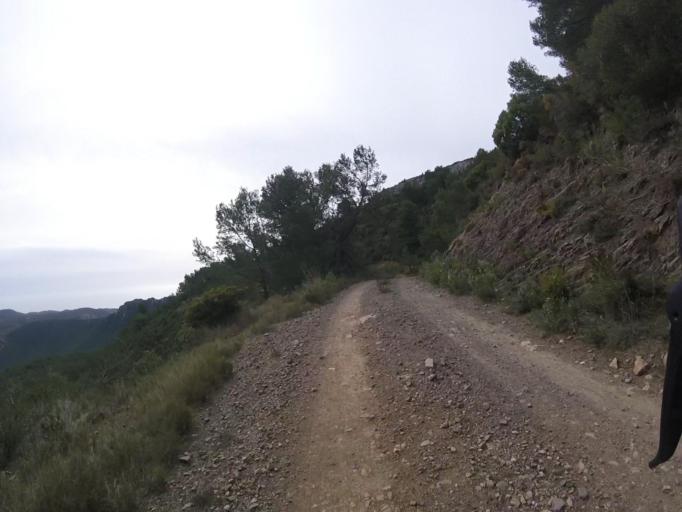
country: ES
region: Valencia
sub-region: Provincia de Castello
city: Benicassim
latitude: 40.0880
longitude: 0.0374
